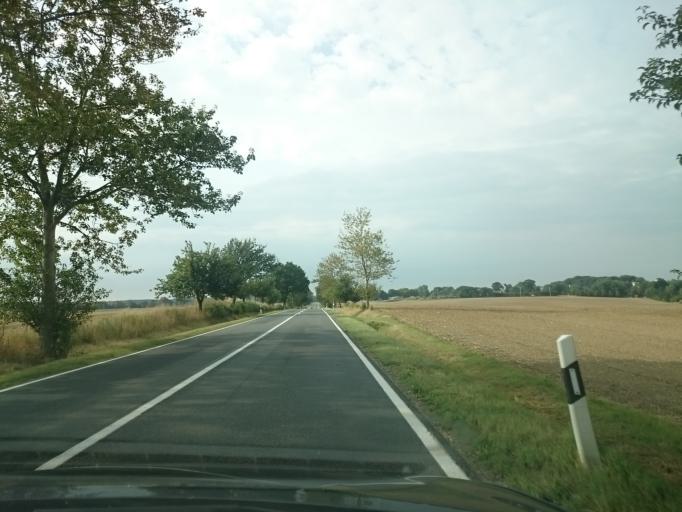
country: DE
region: Mecklenburg-Vorpommern
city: Mollenhagen
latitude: 53.5893
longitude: 12.8689
